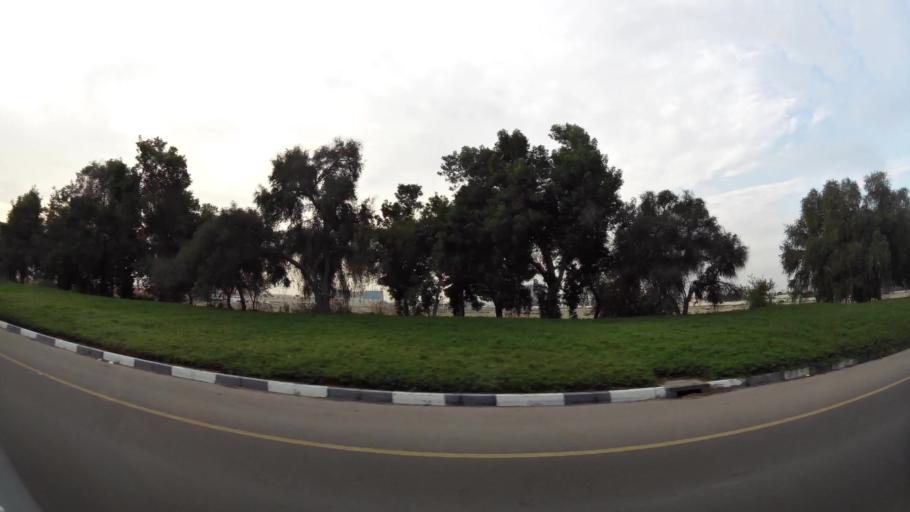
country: AE
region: Abu Dhabi
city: Abu Dhabi
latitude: 24.3894
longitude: 54.5359
